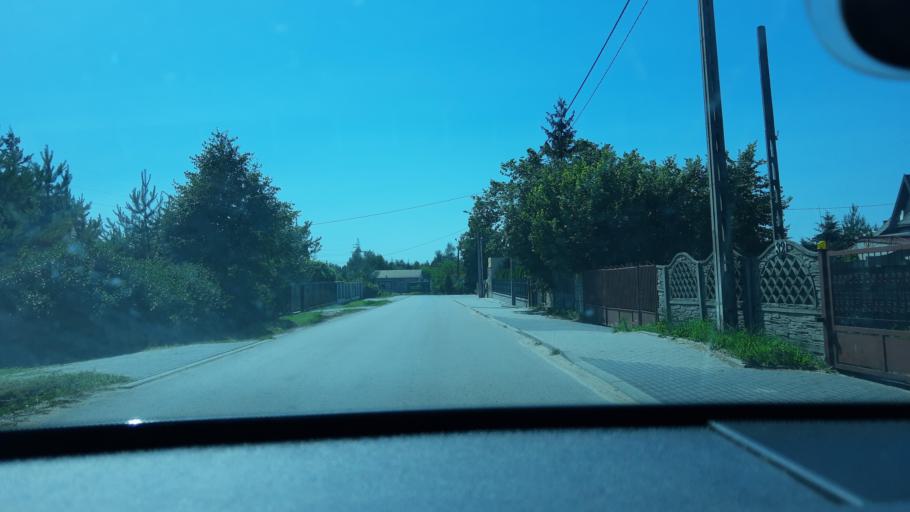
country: PL
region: Lodz Voivodeship
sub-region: Powiat zdunskowolski
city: Zdunska Wola
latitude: 51.6168
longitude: 18.9670
